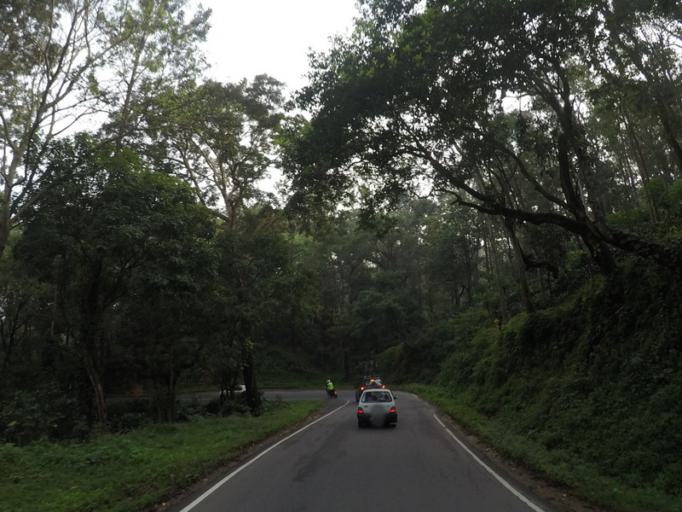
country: IN
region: Karnataka
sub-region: Chikmagalur
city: Mudigere
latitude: 13.2651
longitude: 75.6247
